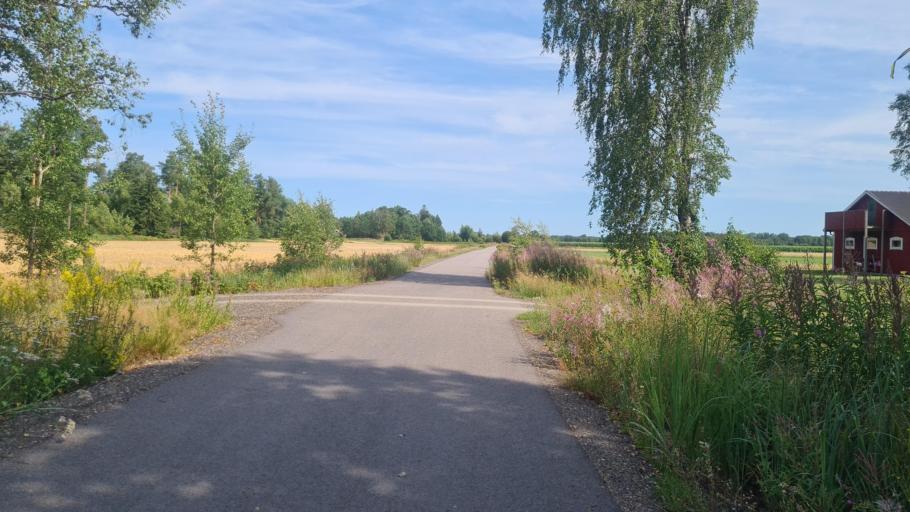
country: SE
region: Kronoberg
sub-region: Ljungby Kommun
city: Lagan
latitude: 56.8945
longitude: 13.9858
